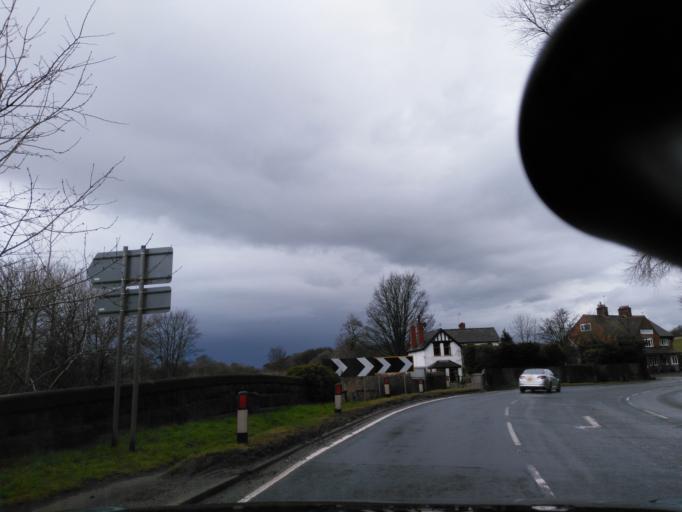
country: GB
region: England
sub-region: North Yorkshire
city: Ripon
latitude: 54.0792
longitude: -1.5351
